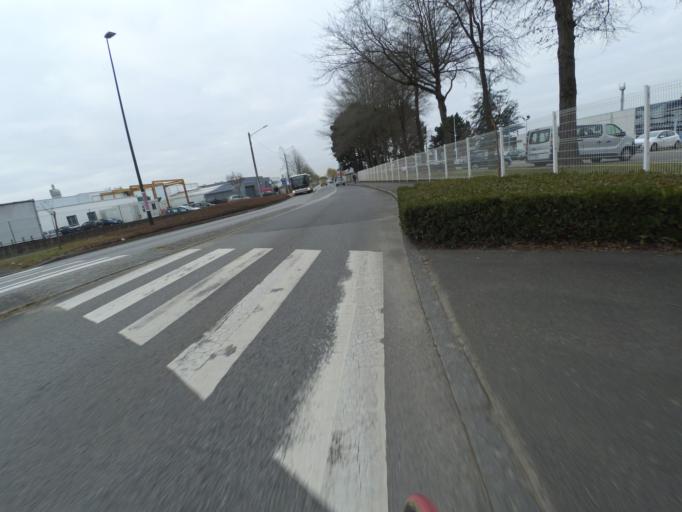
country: FR
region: Pays de la Loire
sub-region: Departement de la Loire-Atlantique
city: Sainte-Luce-sur-Loire
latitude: 47.2672
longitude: -1.4892
